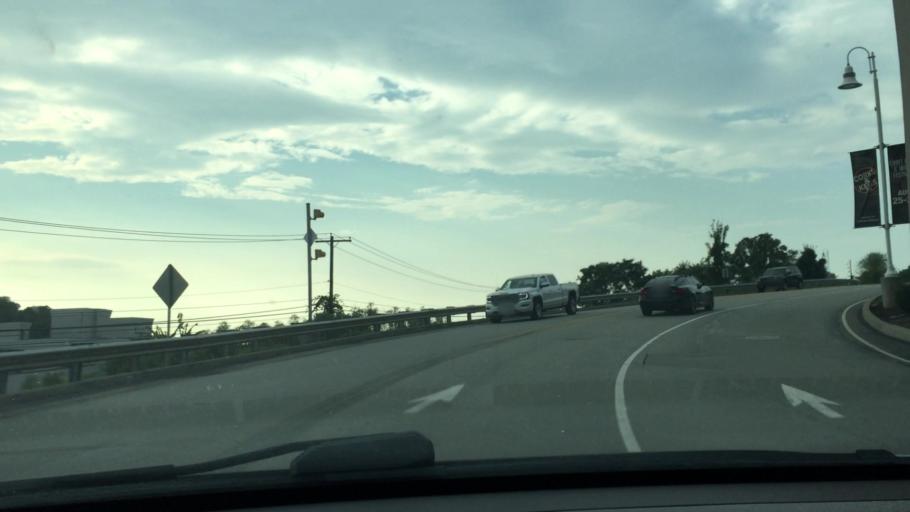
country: US
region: Pennsylvania
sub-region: Washington County
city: McGovern
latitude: 40.2186
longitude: -80.2026
